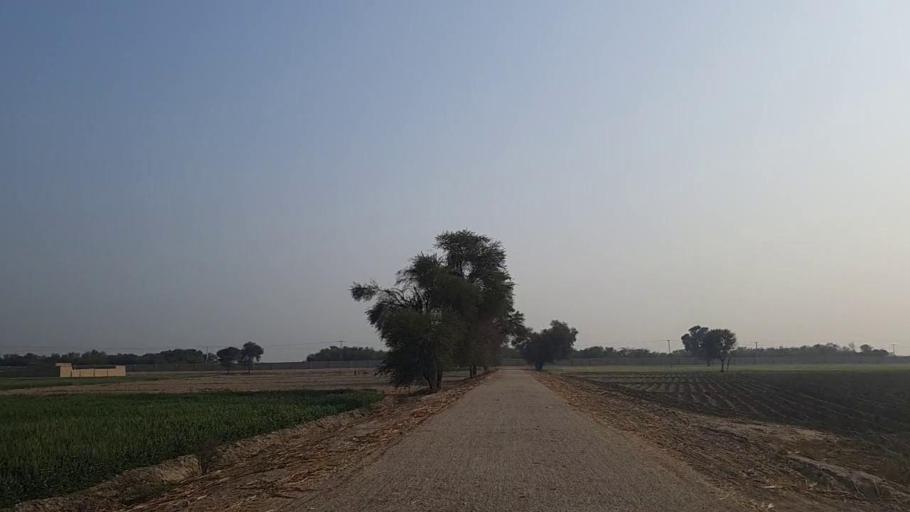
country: PK
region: Sindh
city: Sann
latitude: 26.1116
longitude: 68.1722
